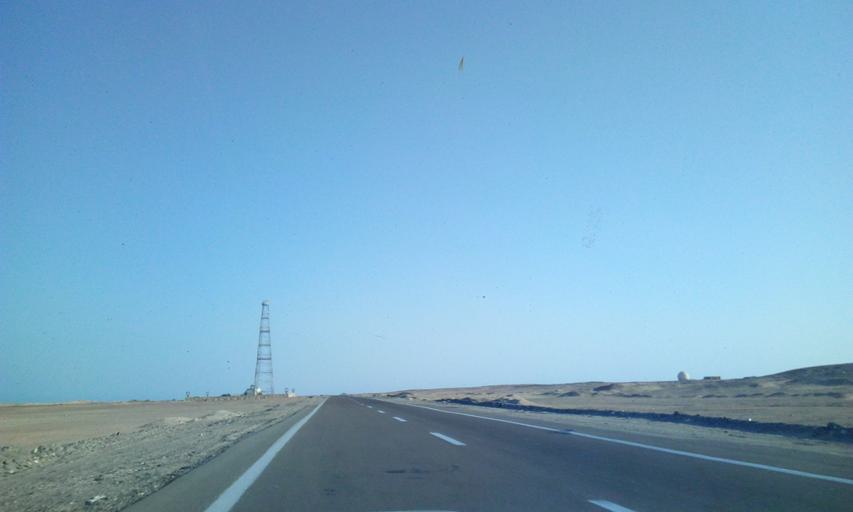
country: EG
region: South Sinai
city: Tor
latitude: 28.6907
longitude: 32.8306
